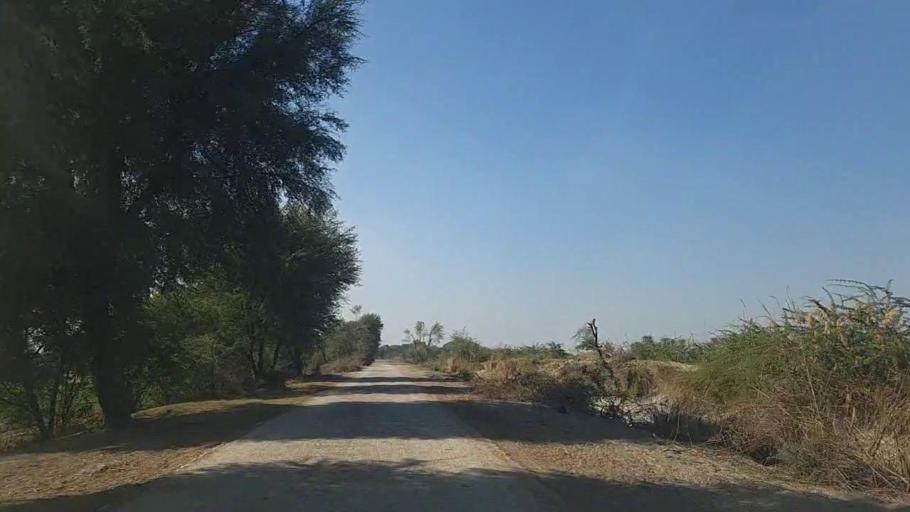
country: PK
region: Sindh
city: Shahpur Chakar
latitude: 26.2131
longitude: 68.6117
